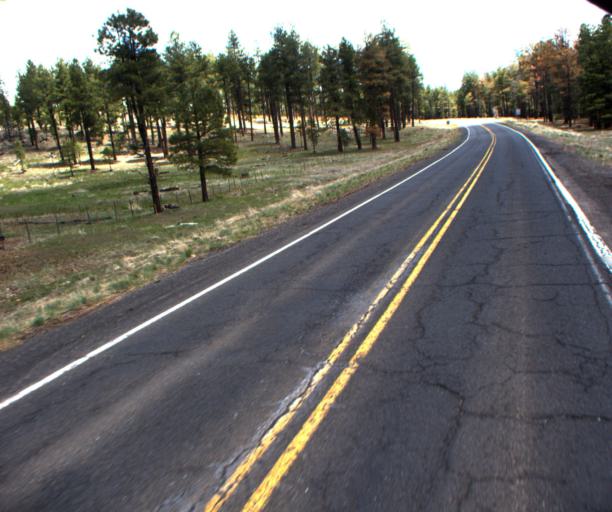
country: US
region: Arizona
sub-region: Coconino County
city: Kachina Village
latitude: 35.1224
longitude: -111.6992
